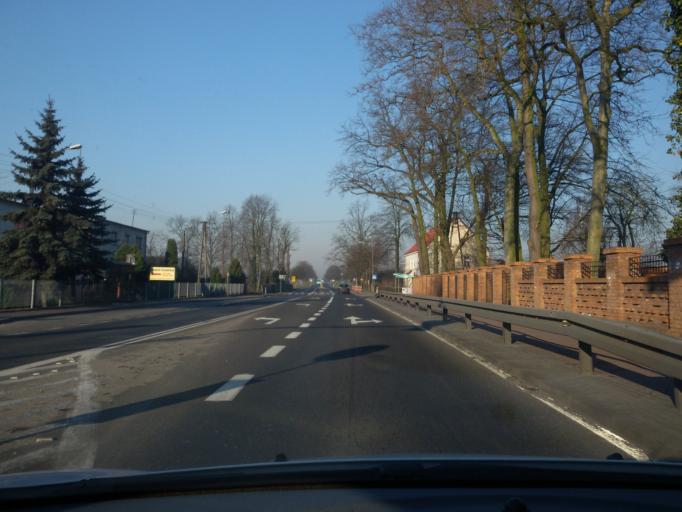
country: PL
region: Greater Poland Voivodeship
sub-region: Powiat leszczynski
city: Swieciechowa
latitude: 51.8247
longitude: 16.4441
